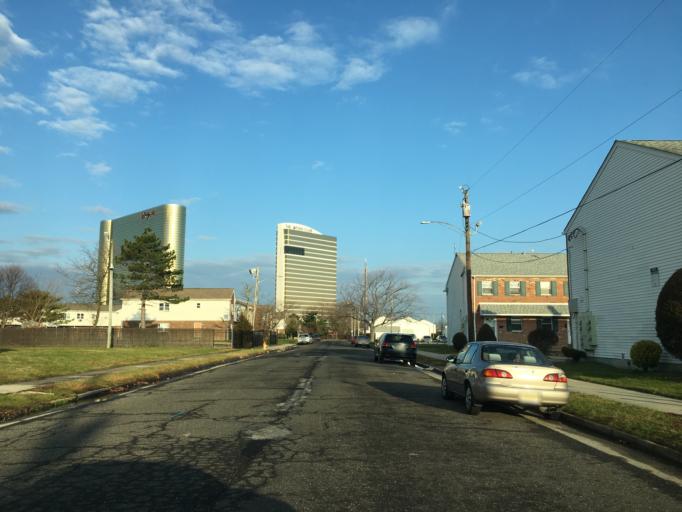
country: US
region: New Jersey
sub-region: Atlantic County
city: Atlantic City
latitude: 39.3732
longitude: -74.4291
